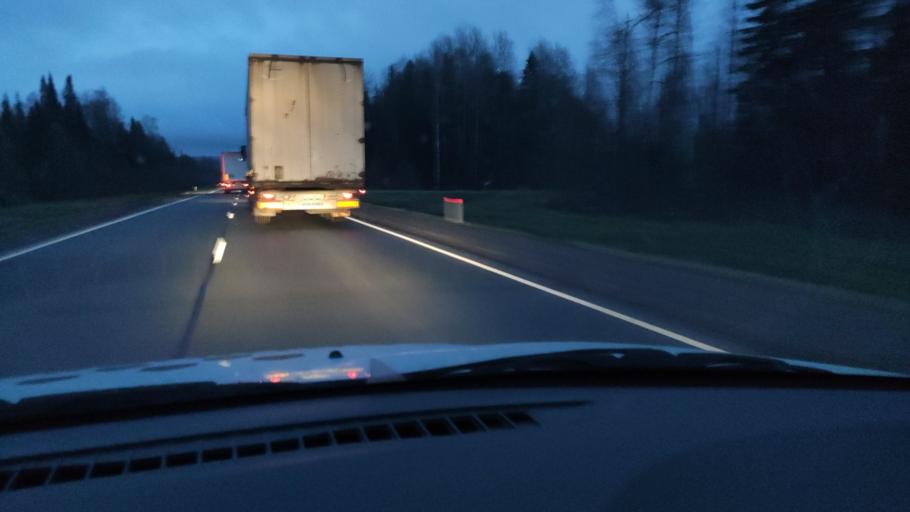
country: RU
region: Kirov
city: Kostino
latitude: 58.8314
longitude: 53.5173
